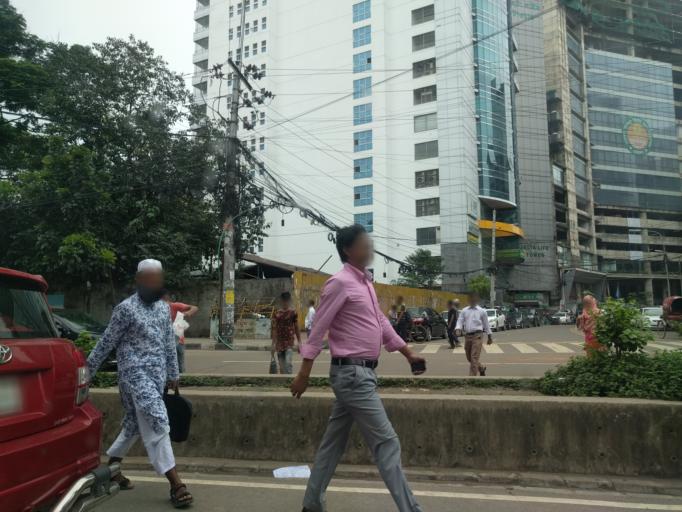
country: BD
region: Dhaka
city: Paltan
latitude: 23.7955
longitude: 90.4138
